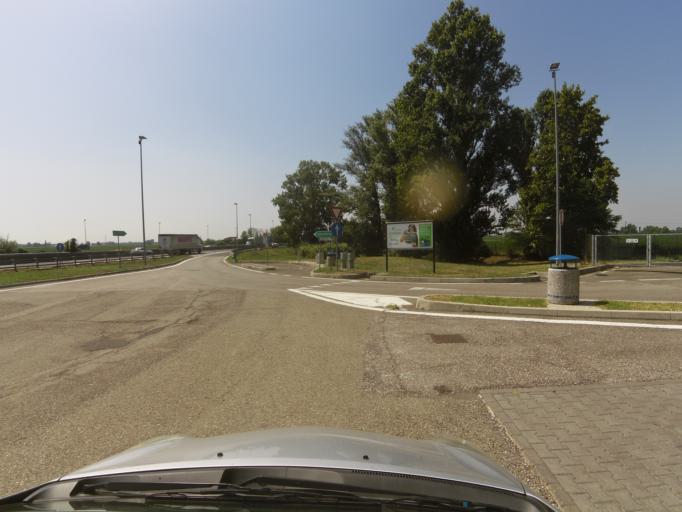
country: IT
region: Veneto
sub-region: Provincia di Rovigo
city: Costa di Rovigo
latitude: 45.0412
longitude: 11.7092
